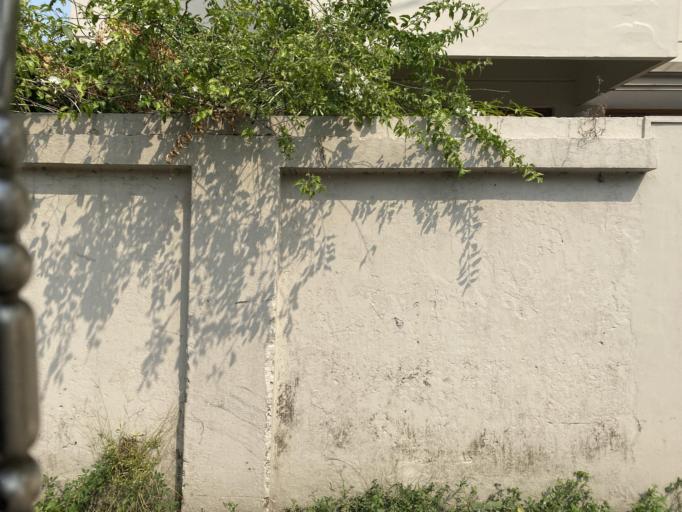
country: IN
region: Kerala
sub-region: Ernakulam
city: Cochin
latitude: 9.9538
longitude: 76.2445
